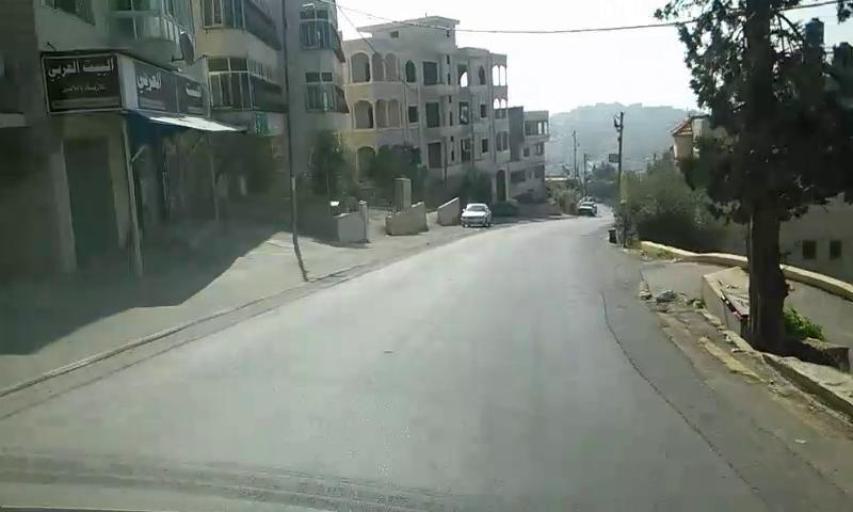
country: PS
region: West Bank
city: Dayr Jarir
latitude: 31.9642
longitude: 35.2938
